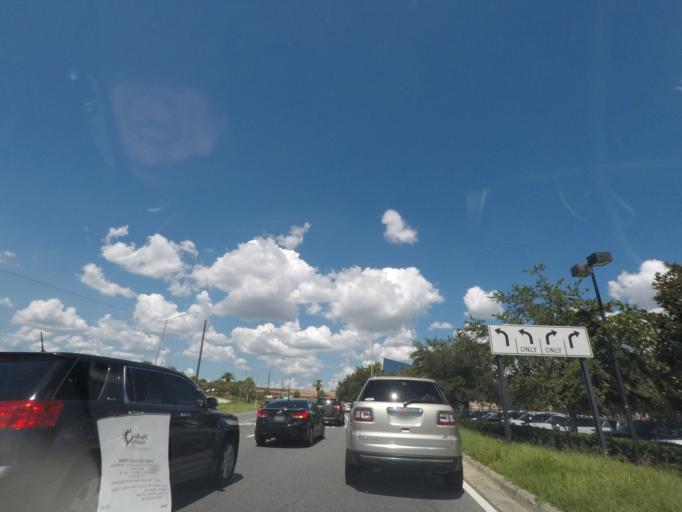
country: US
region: Florida
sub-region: Orange County
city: Oak Ridge
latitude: 28.4908
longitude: -81.4324
